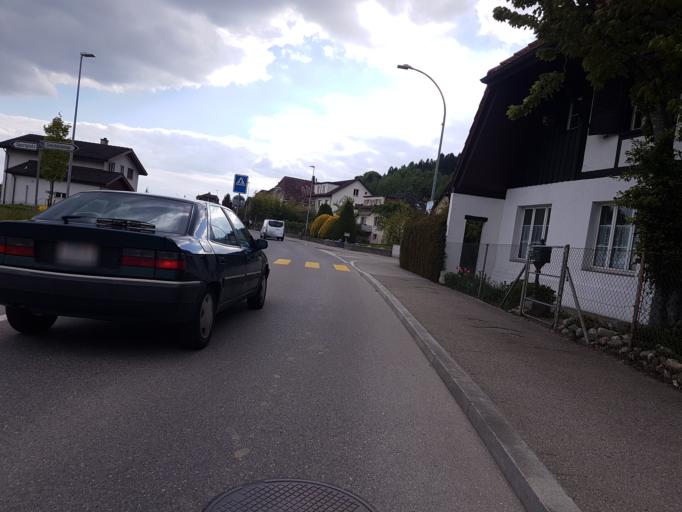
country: CH
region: Bern
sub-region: Biel/Bienne District
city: Orpund
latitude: 47.1478
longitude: 7.3201
